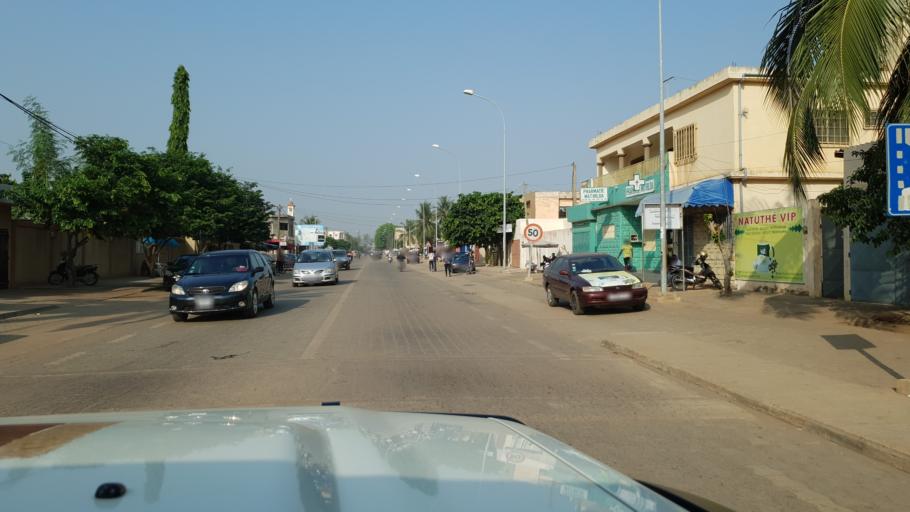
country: TG
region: Maritime
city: Lome
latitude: 6.1823
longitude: 1.2004
